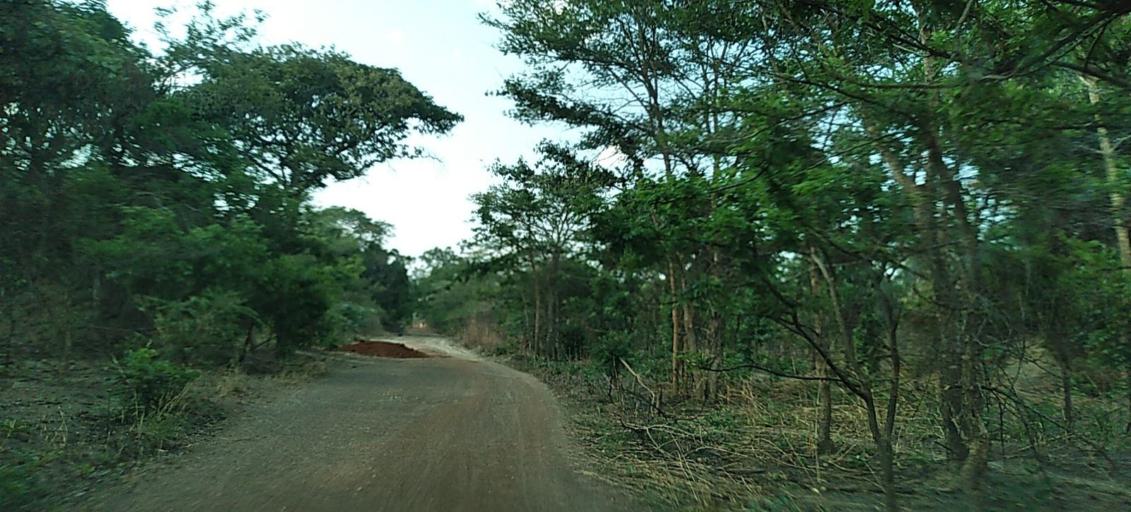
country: ZM
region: Copperbelt
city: Mpongwe
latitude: -13.4647
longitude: 28.0690
